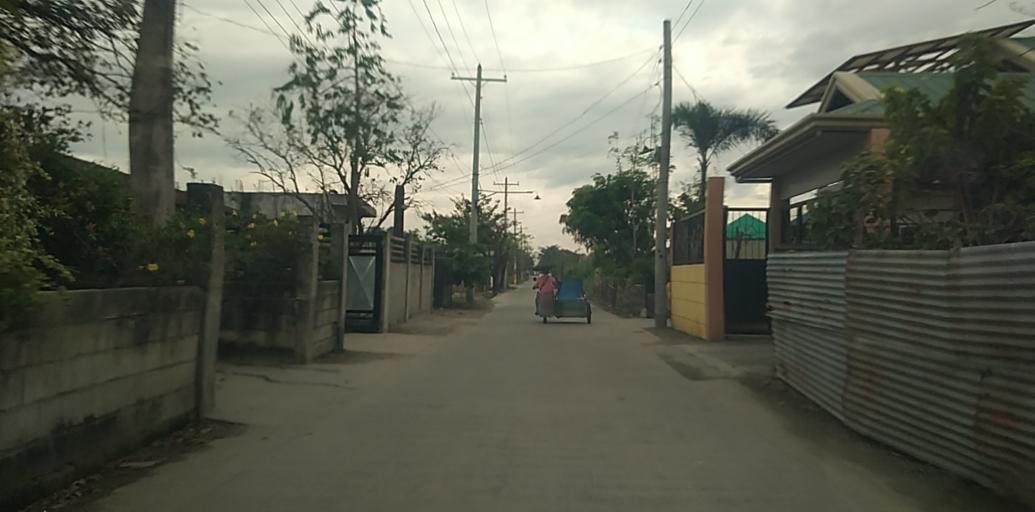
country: PH
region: Central Luzon
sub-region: Province of Pampanga
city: San Fernando
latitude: 15.0089
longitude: 120.7035
